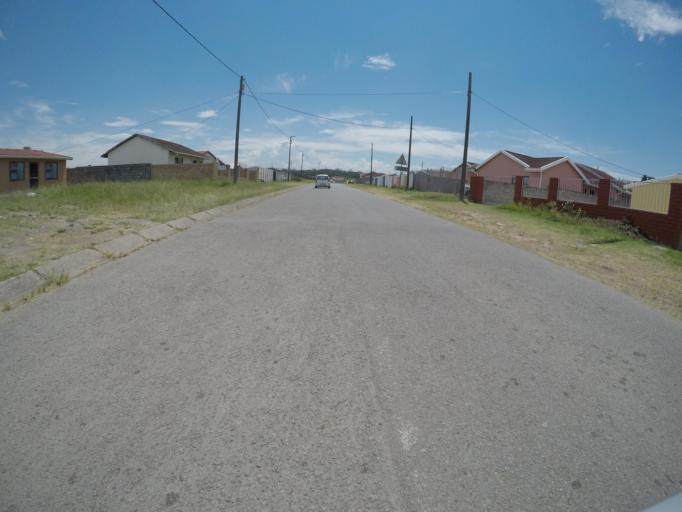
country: ZA
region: Eastern Cape
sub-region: Buffalo City Metropolitan Municipality
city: East London
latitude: -33.0470
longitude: 27.8498
